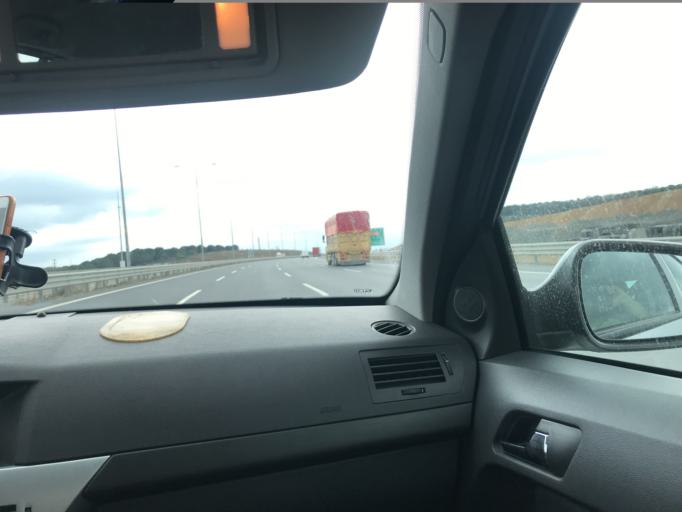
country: TR
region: Istanbul
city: Sultanbeyli
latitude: 40.9946
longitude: 29.3208
